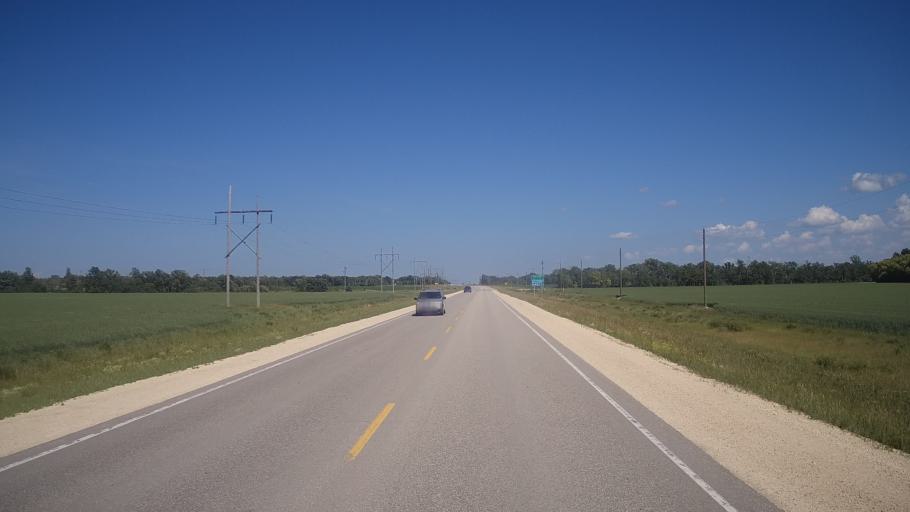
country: CA
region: Manitoba
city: Stonewall
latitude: 50.1228
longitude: -97.3495
